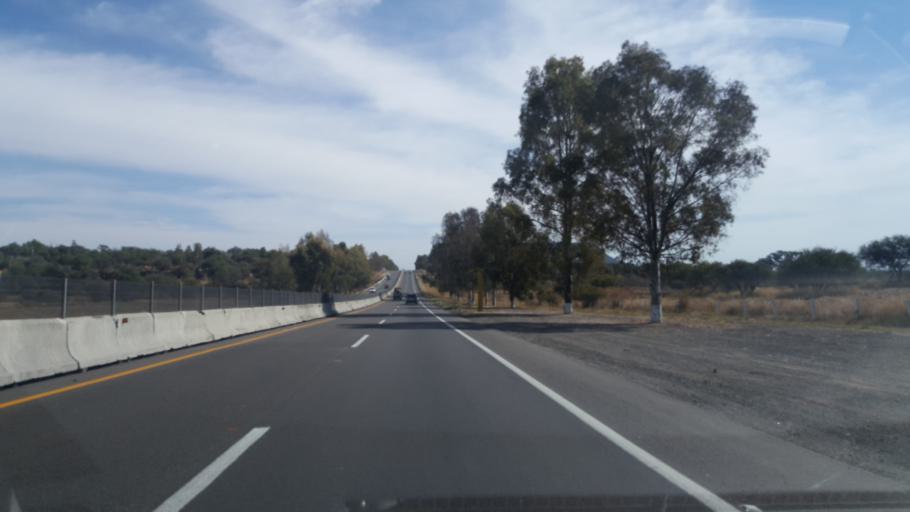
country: MX
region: Jalisco
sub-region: Lagos de Moreno
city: Cristeros [Fraccionamiento]
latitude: 21.3120
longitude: -102.0336
